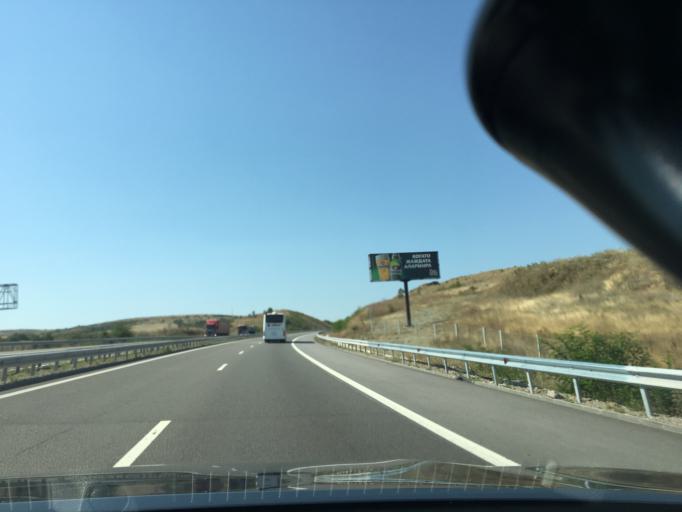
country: BG
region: Kyustendil
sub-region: Obshtina Dupnitsa
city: Dupnitsa
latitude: 42.3014
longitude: 23.0941
